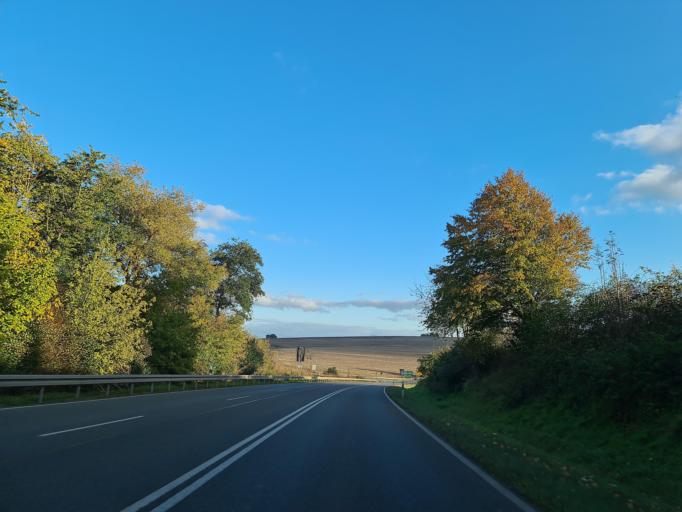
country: DE
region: Thuringia
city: Teichwitz
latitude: 50.7683
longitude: 12.0859
